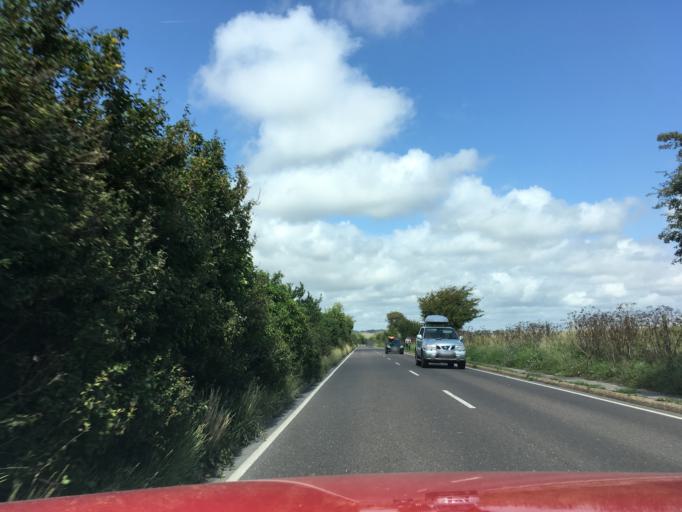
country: GB
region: England
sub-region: East Sussex
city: Rye
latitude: 50.9358
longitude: 0.7252
